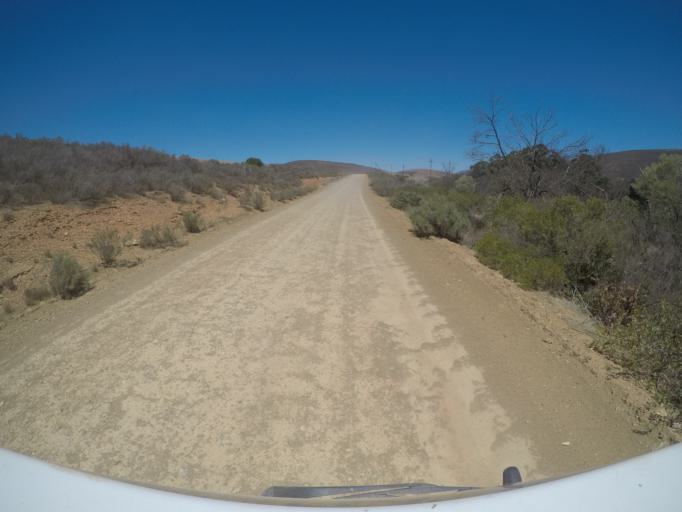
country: ZA
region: Western Cape
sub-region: Overberg District Municipality
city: Caledon
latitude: -34.1399
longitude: 19.2480
